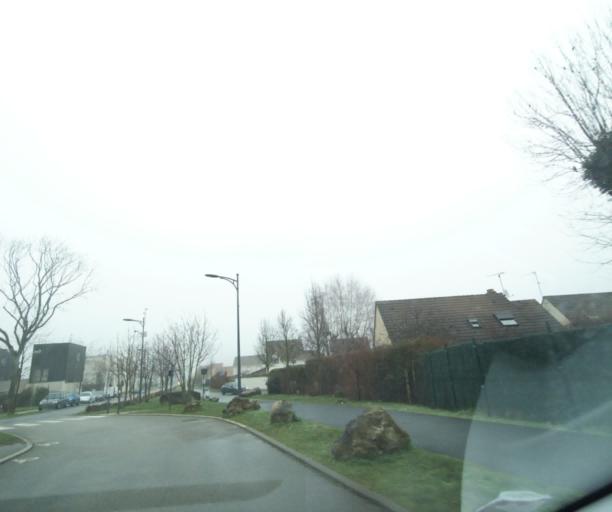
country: FR
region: Ile-de-France
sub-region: Departement de Seine-et-Marne
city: Dammartin-en-Goele
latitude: 49.0607
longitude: 2.6770
